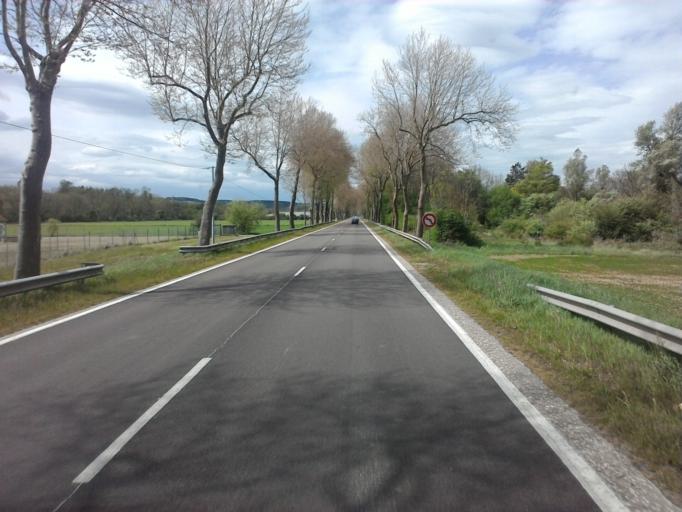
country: FR
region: Bourgogne
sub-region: Departement de l'Yonne
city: Champs-sur-Yonne
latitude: 47.7152
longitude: 3.6182
